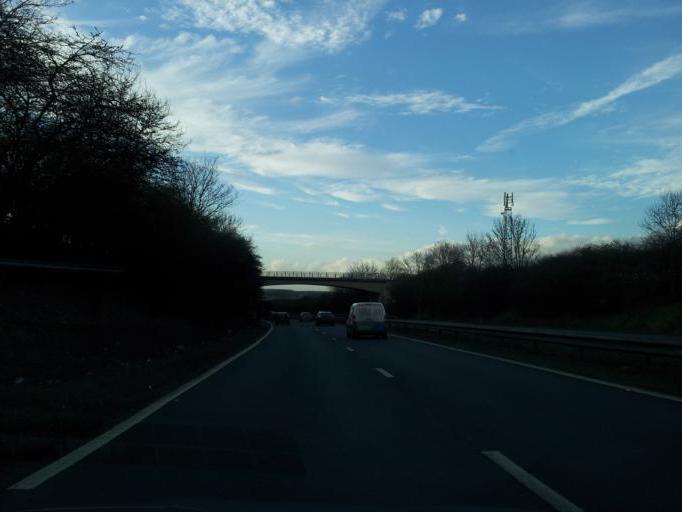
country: GB
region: England
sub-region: Lincolnshire
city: Stamford
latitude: 52.6355
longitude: -0.4787
